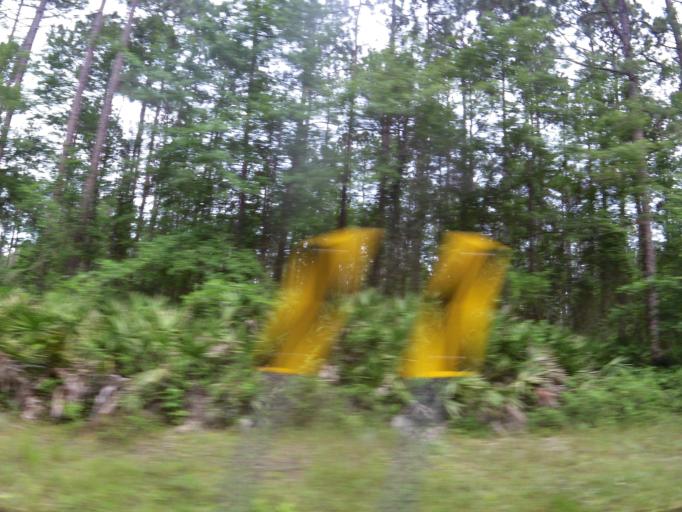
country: US
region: Florida
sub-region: Nassau County
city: Nassau Village-Ratliff
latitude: 30.5318
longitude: -81.7269
